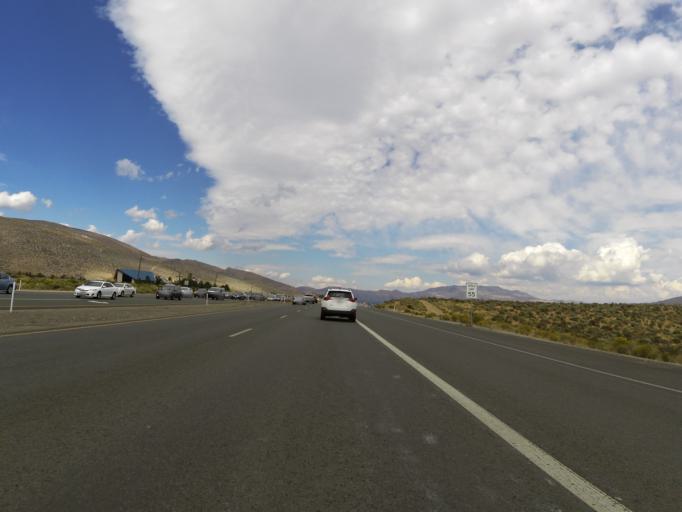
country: US
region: Nevada
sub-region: Douglas County
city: Indian Hills
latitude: 39.1026
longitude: -119.7746
